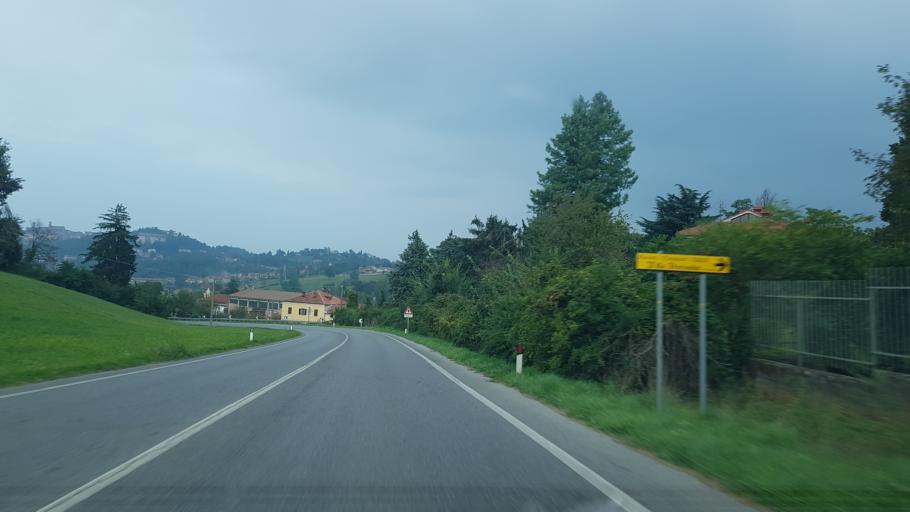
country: IT
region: Piedmont
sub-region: Provincia di Cuneo
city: Mondovi
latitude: 44.3719
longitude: 7.8046
